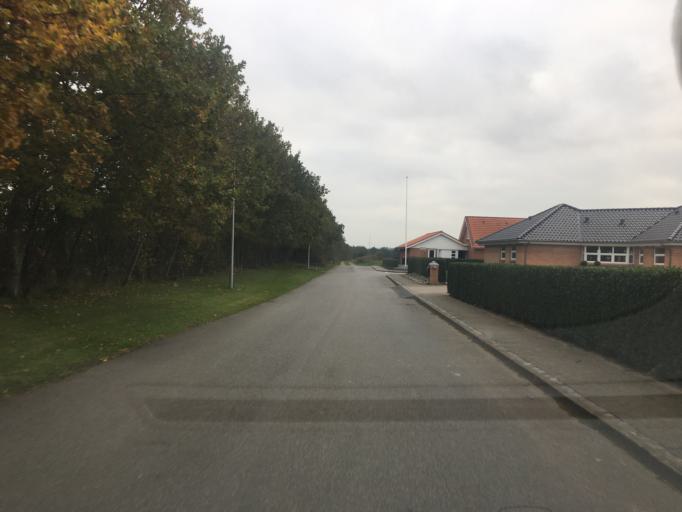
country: DK
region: South Denmark
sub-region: Tonder Kommune
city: Tonder
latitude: 54.9777
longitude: 8.8732
